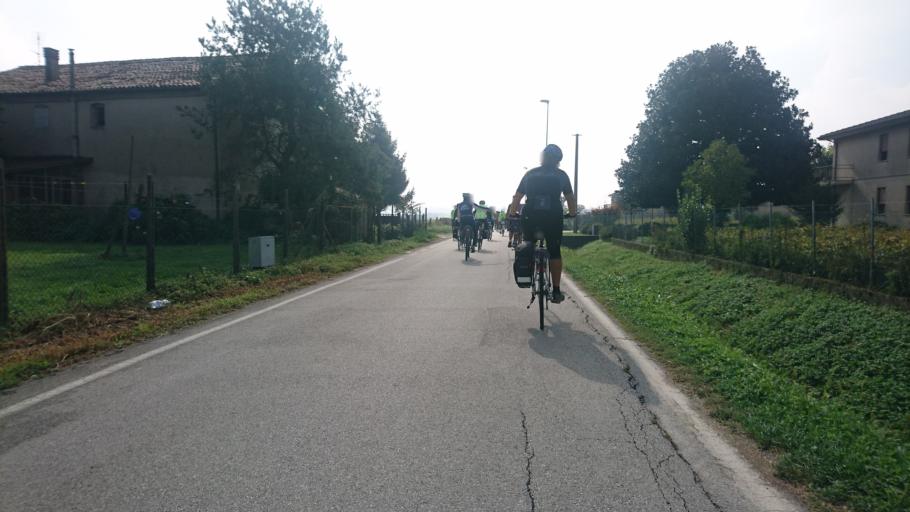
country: IT
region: Veneto
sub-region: Provincia di Padova
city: Boara Pisani
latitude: 45.1210
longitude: 11.7830
